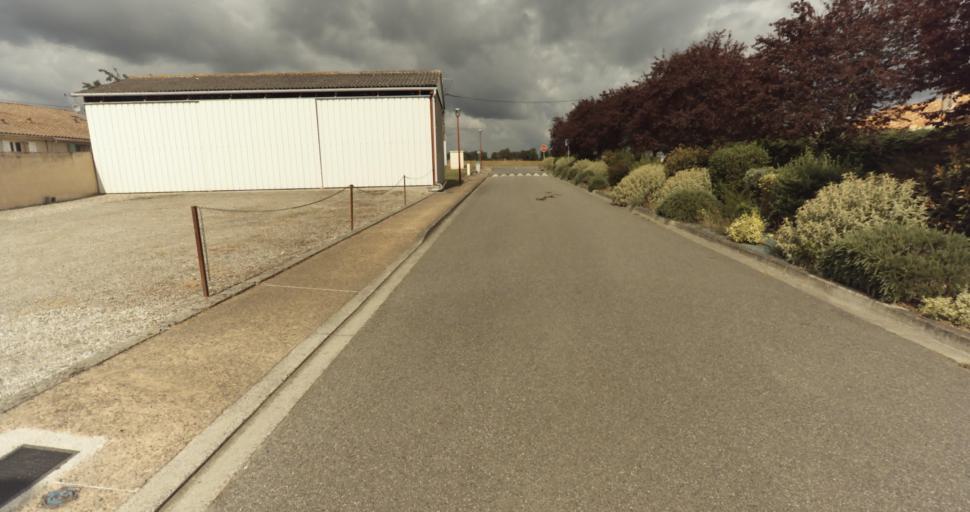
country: FR
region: Midi-Pyrenees
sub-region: Departement de la Haute-Garonne
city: Fonsorbes
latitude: 43.5551
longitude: 1.2272
